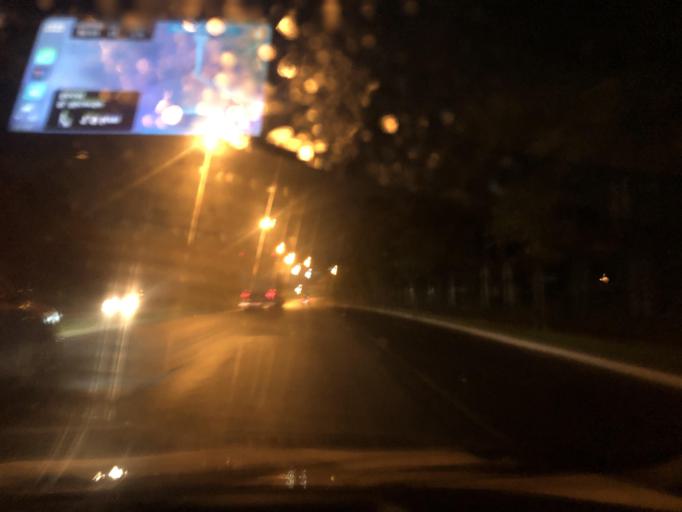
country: BR
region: Santa Catarina
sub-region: Joinville
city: Joinville
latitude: -26.3805
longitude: -48.8442
